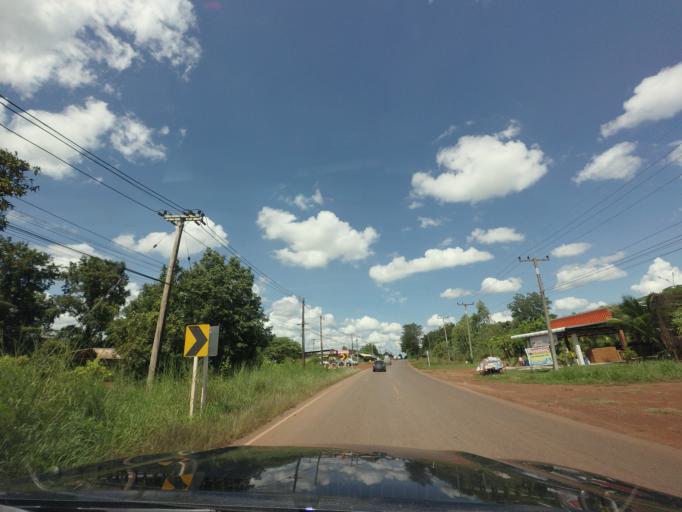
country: TH
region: Changwat Udon Thani
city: Ban Dung
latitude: 17.7372
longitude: 103.2543
